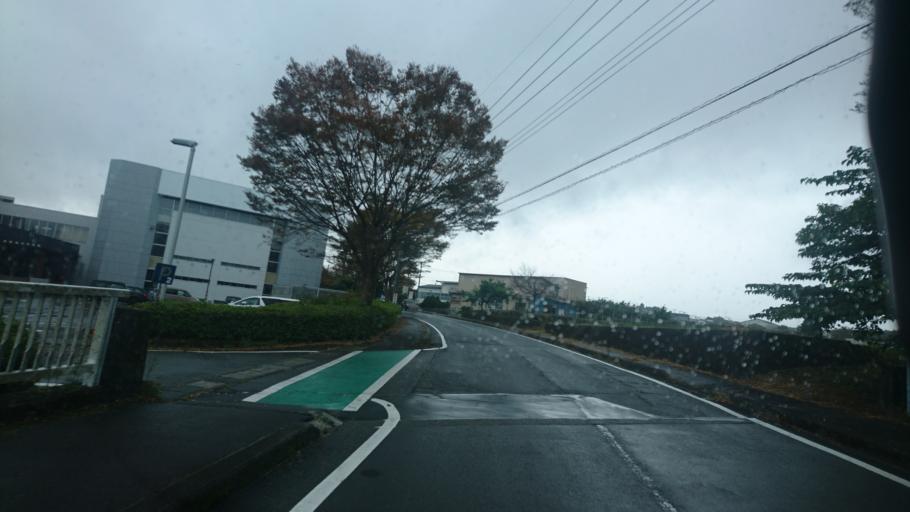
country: JP
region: Shizuoka
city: Gotemba
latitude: 35.3153
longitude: 138.9126
